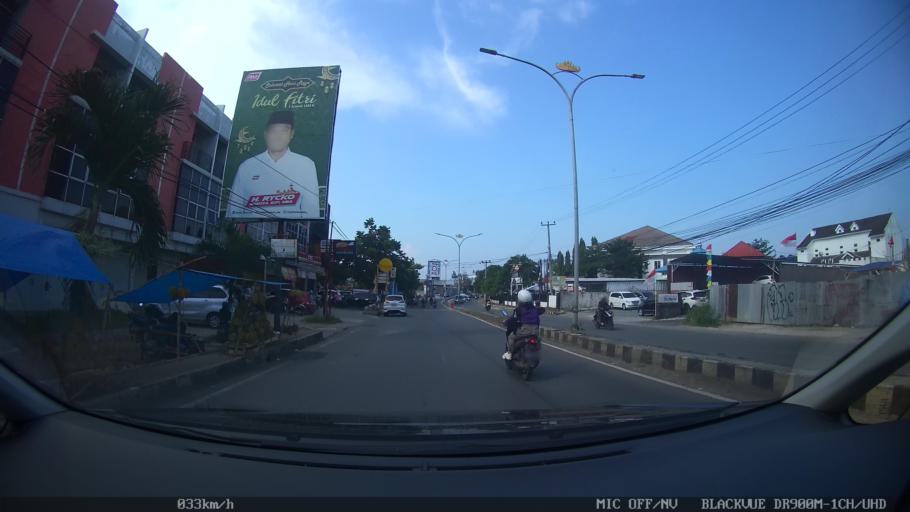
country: ID
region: Lampung
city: Kedaton
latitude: -5.3755
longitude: 105.2224
